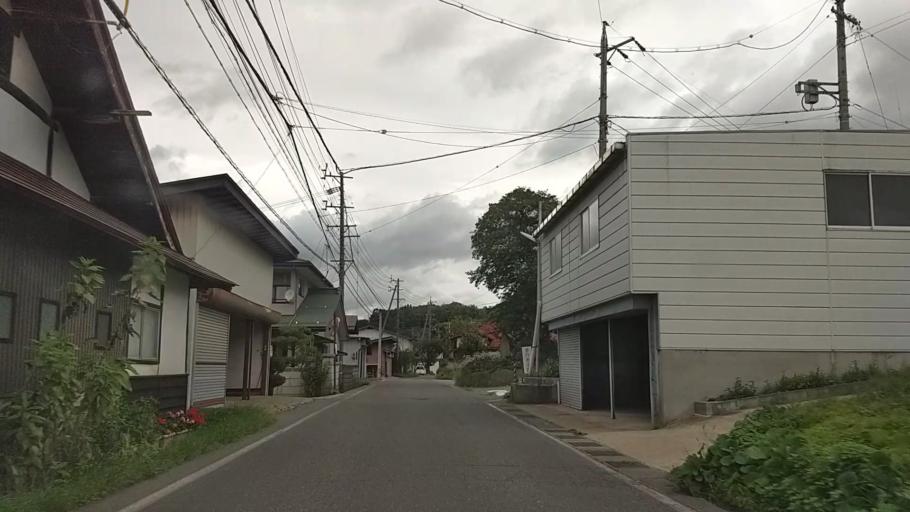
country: JP
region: Nagano
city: Iiyama
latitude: 36.8055
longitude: 138.3598
